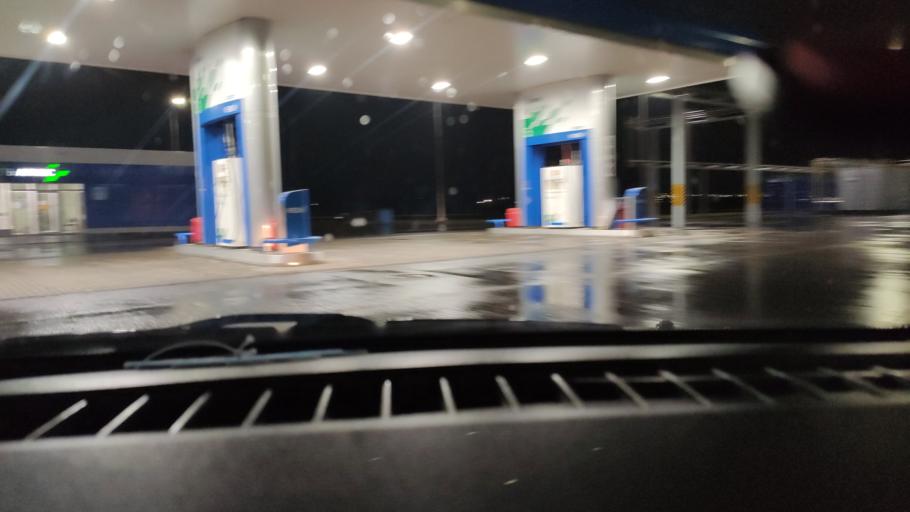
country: RU
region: Udmurtiya
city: Votkinsk
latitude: 57.0361
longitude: 54.0252
